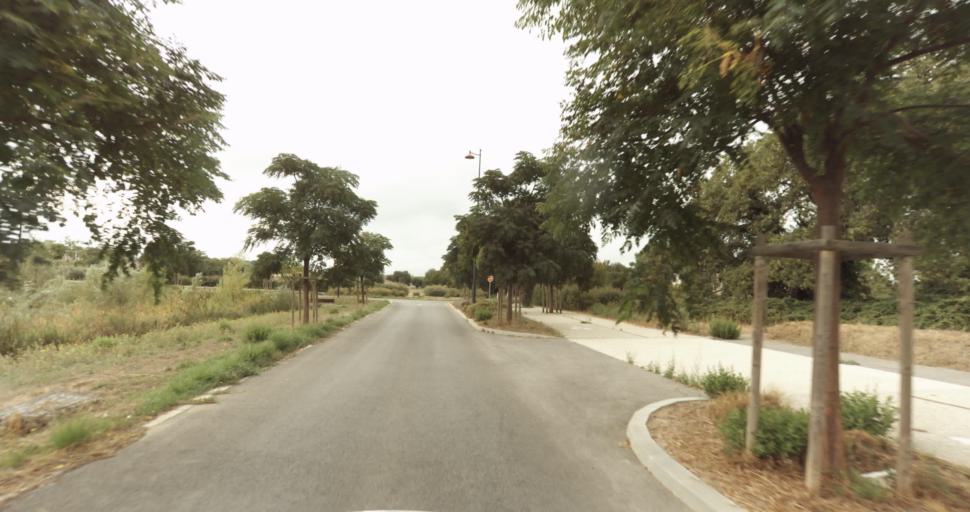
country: FR
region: Provence-Alpes-Cote d'Azur
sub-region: Departement des Bouches-du-Rhone
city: Saint-Victoret
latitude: 43.4138
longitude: 5.2576
